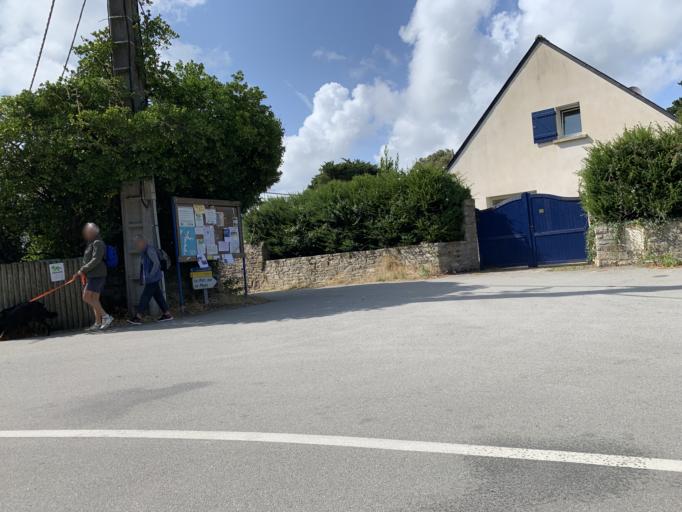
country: FR
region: Brittany
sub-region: Departement du Morbihan
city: Arradon
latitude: 47.5955
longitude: -2.8496
